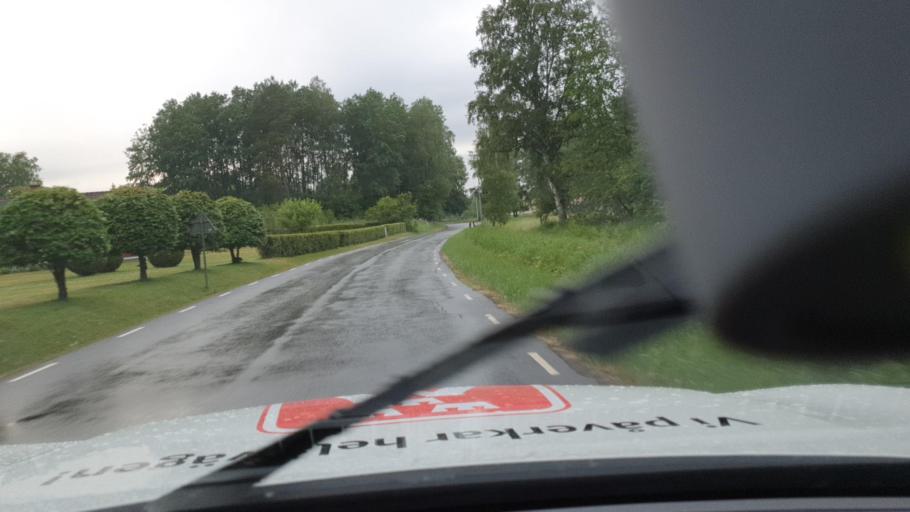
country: SE
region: Vaestra Goetaland
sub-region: Skovde Kommun
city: Stopen
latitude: 58.4224
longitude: 13.9105
